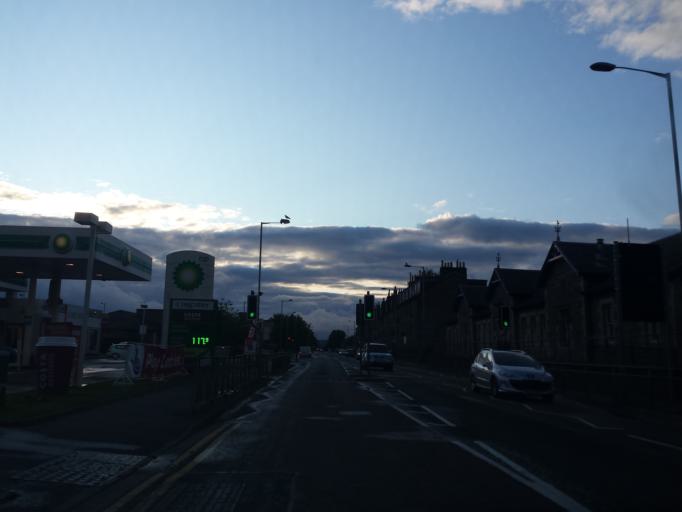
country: GB
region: Scotland
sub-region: Perth and Kinross
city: Perth
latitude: 56.4000
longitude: -3.4374
